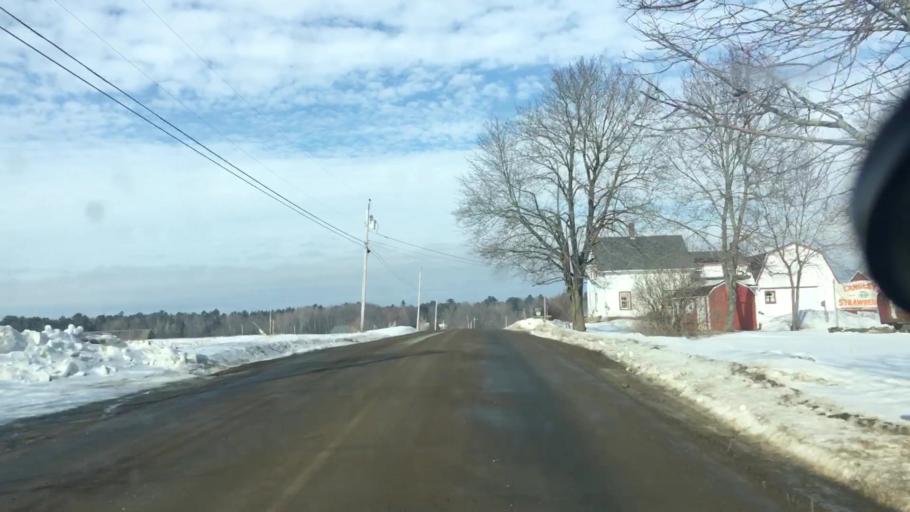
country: US
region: Maine
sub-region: Penobscot County
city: Levant
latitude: 44.8578
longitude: -68.8785
